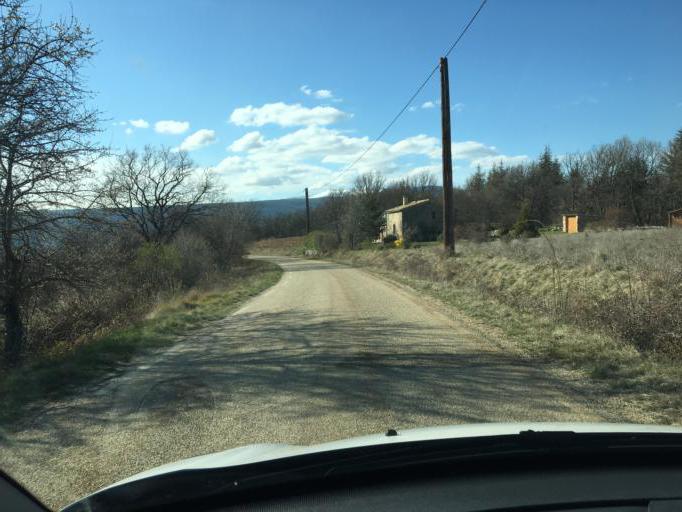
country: FR
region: Provence-Alpes-Cote d'Azur
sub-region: Departement du Vaucluse
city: Sault
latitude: 44.0820
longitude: 5.4146
